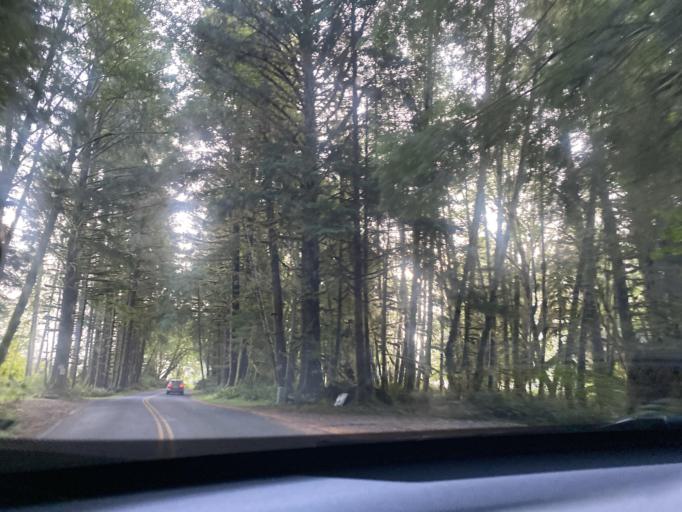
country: US
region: Washington
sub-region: Clallam County
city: Forks
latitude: 47.8170
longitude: -124.0423
